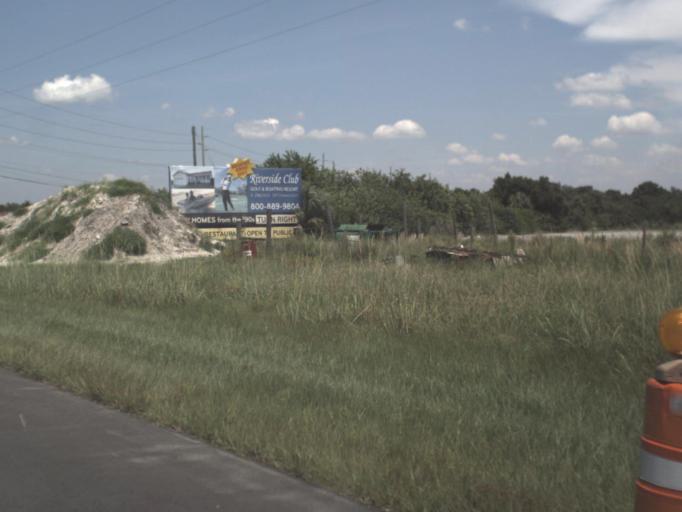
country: US
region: Florida
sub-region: Hillsborough County
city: Ruskin
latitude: 27.6831
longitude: -82.4740
